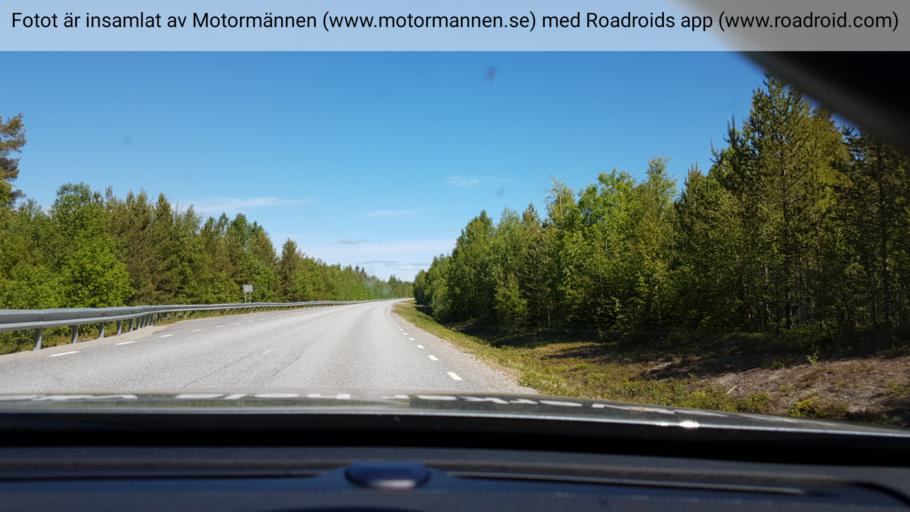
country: SE
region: Vaesterbotten
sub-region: Vilhelmina Kommun
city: Vilhelmina
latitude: 64.4267
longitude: 16.8041
